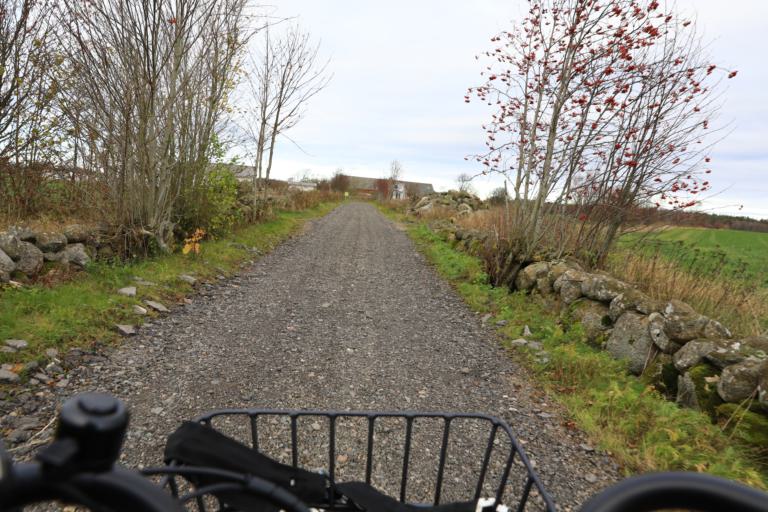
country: SE
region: Halland
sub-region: Varbergs Kommun
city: Traslovslage
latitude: 57.0528
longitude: 12.3381
